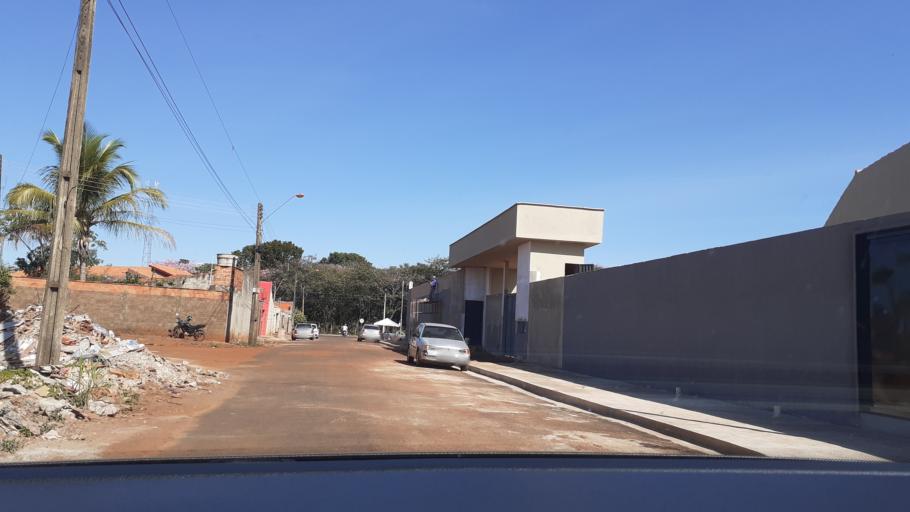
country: BR
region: Goias
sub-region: Itumbiara
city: Itumbiara
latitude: -18.4128
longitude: -49.2584
